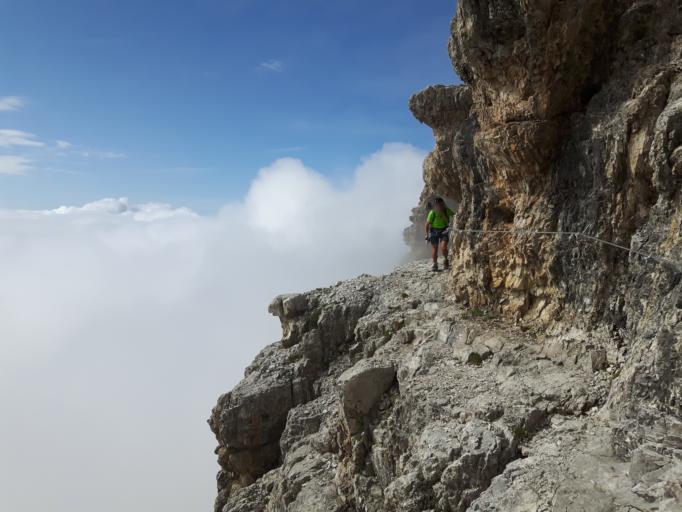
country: IT
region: Trentino-Alto Adige
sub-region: Provincia di Trento
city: San Lorenzo in Banale
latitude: 46.1508
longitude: 10.8764
